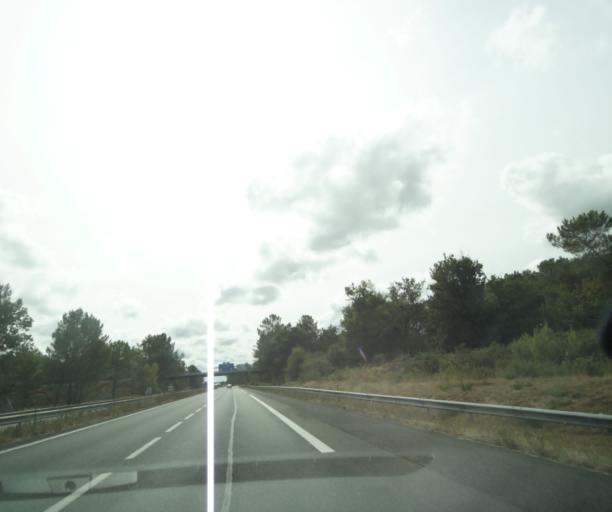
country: FR
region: Aquitaine
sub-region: Departement de la Gironde
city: Marcillac
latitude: 45.2593
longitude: -0.5456
